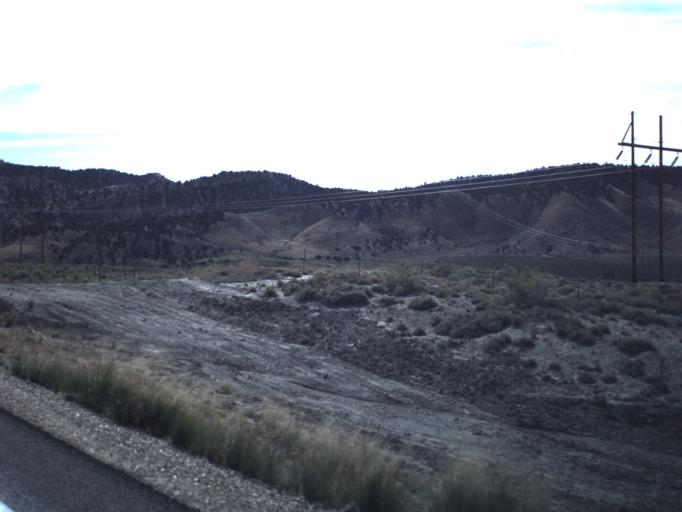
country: US
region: Utah
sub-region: Garfield County
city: Panguitch
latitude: 37.5949
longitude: -111.9427
